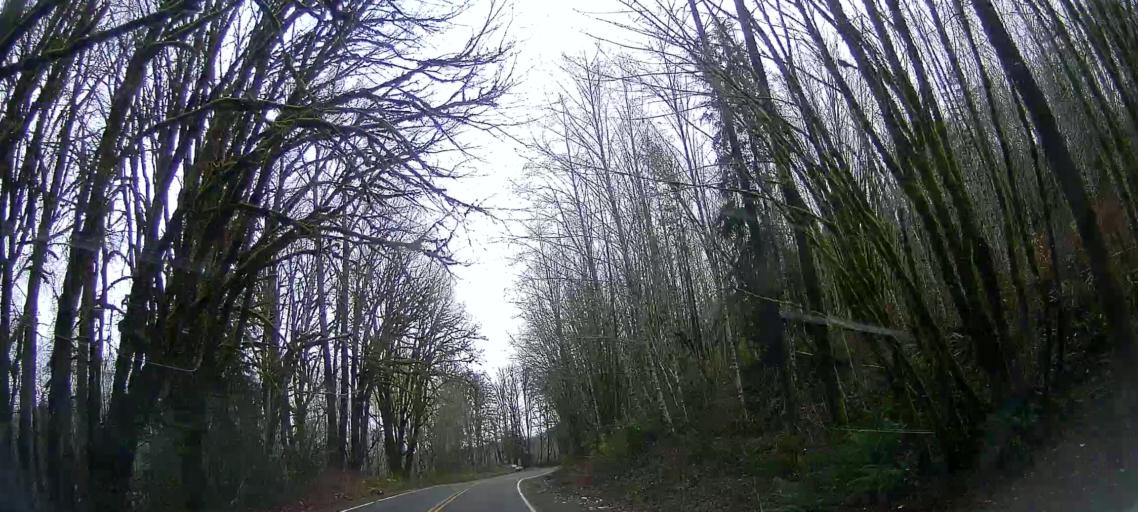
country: US
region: Washington
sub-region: Skagit County
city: Sedro-Woolley
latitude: 48.5114
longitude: -121.9056
